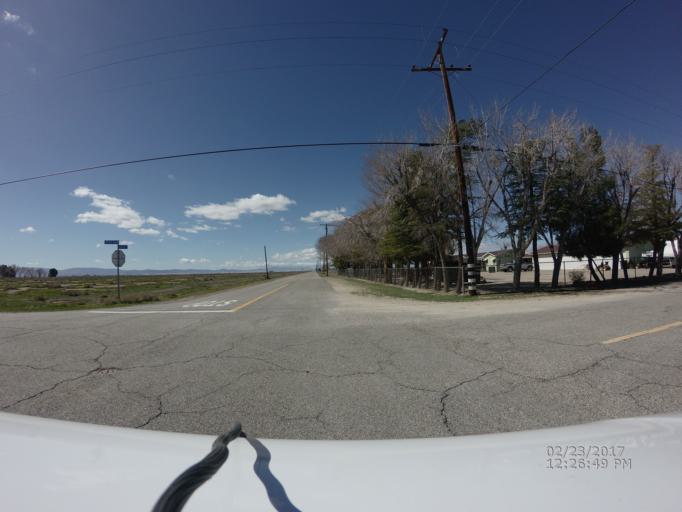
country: US
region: California
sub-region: Los Angeles County
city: Lancaster
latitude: 34.7485
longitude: -118.0234
